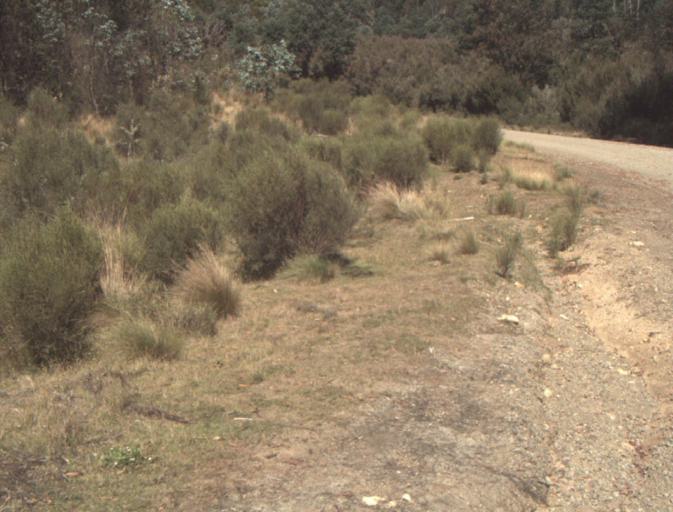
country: AU
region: Tasmania
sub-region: Dorset
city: Scottsdale
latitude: -41.3144
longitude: 147.4638
